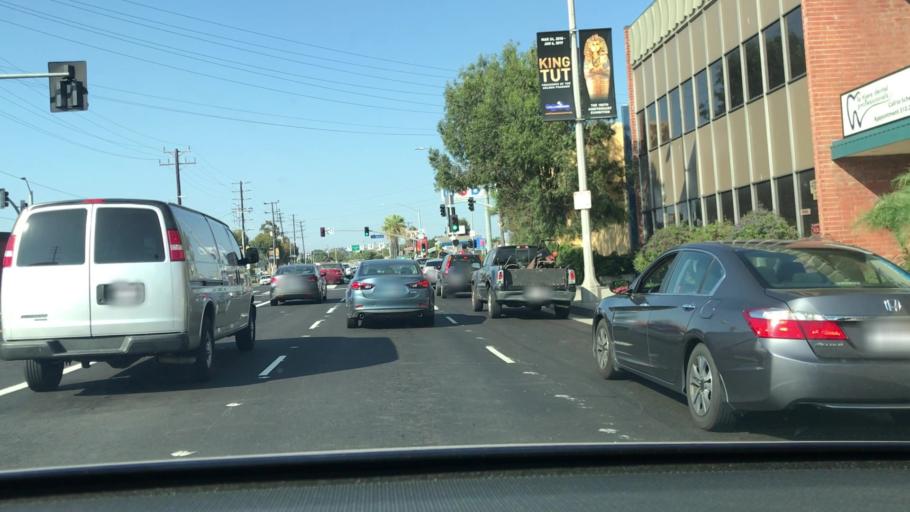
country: US
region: California
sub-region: Los Angeles County
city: Ladera Heights
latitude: 33.9768
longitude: -118.3723
